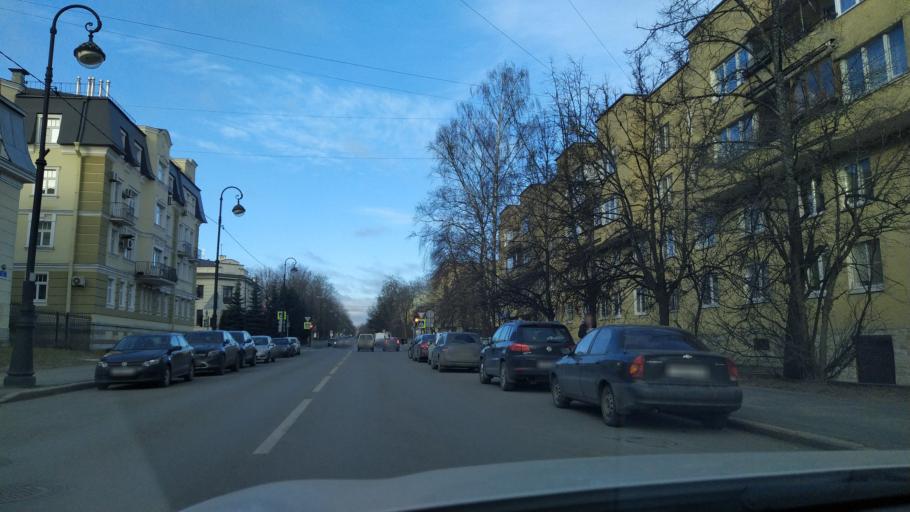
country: RU
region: St.-Petersburg
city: Pushkin
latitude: 59.7191
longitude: 30.4145
